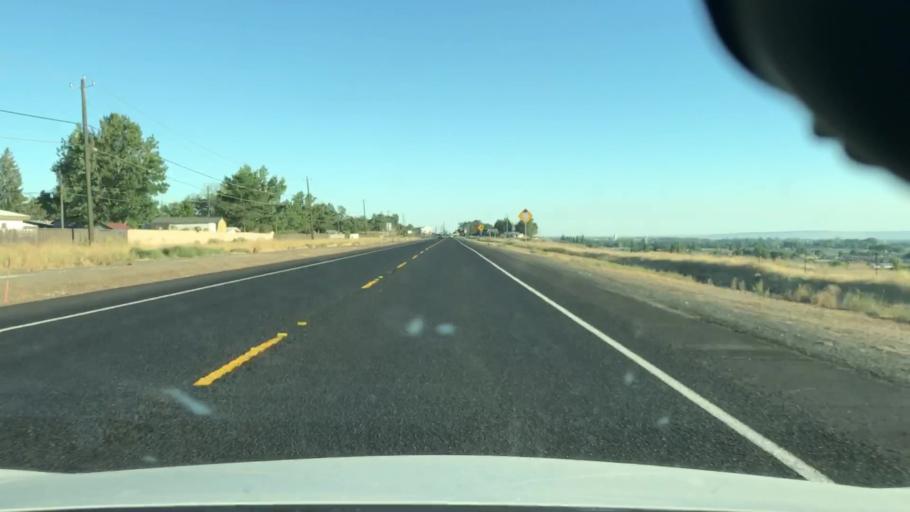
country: US
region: Washington
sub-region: Grant County
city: Moses Lake North
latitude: 47.1681
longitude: -119.3275
